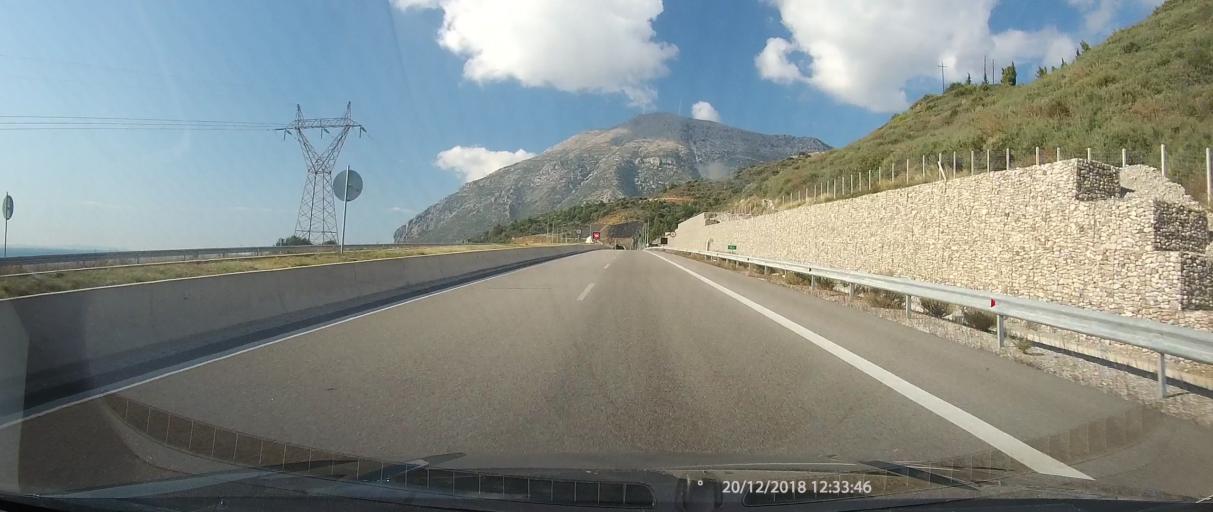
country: GR
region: West Greece
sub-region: Nomos Aitolias kai Akarnanias
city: Antirrio
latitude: 38.3522
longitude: 21.7324
